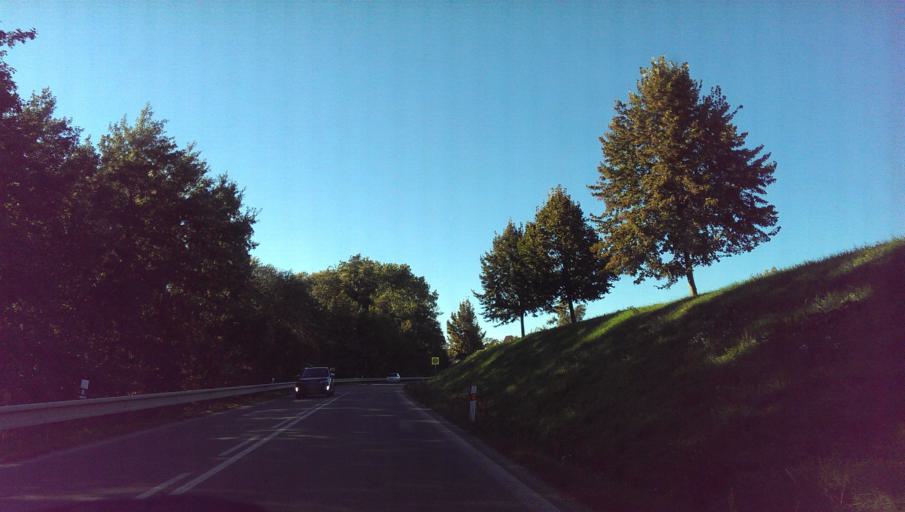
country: CZ
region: Zlin
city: Velehrad
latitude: 49.1008
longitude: 17.4121
